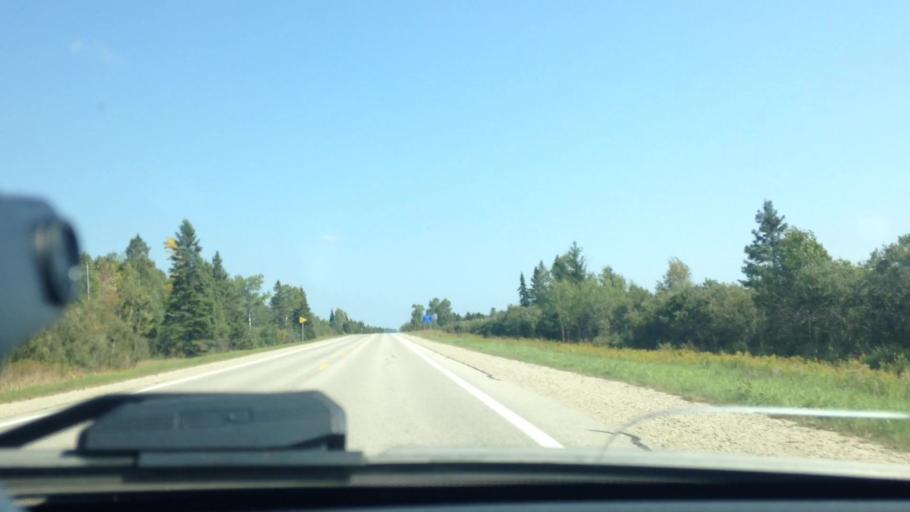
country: US
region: Michigan
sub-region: Luce County
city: Newberry
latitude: 46.3104
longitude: -85.6034
